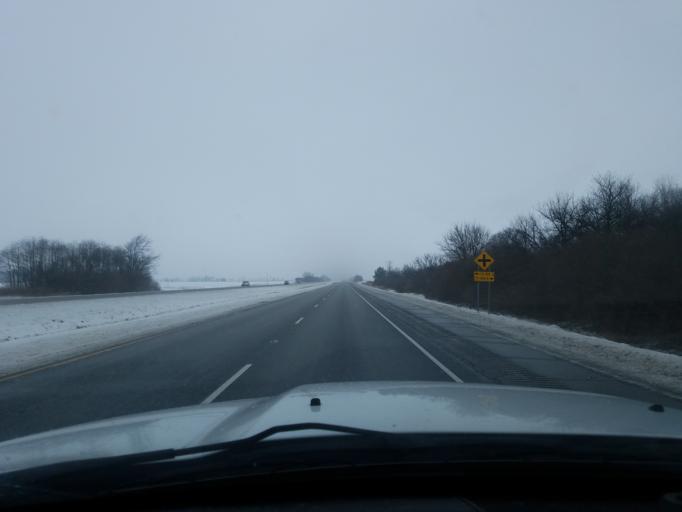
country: US
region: Indiana
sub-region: Fulton County
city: Rochester
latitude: 40.9782
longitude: -86.1679
